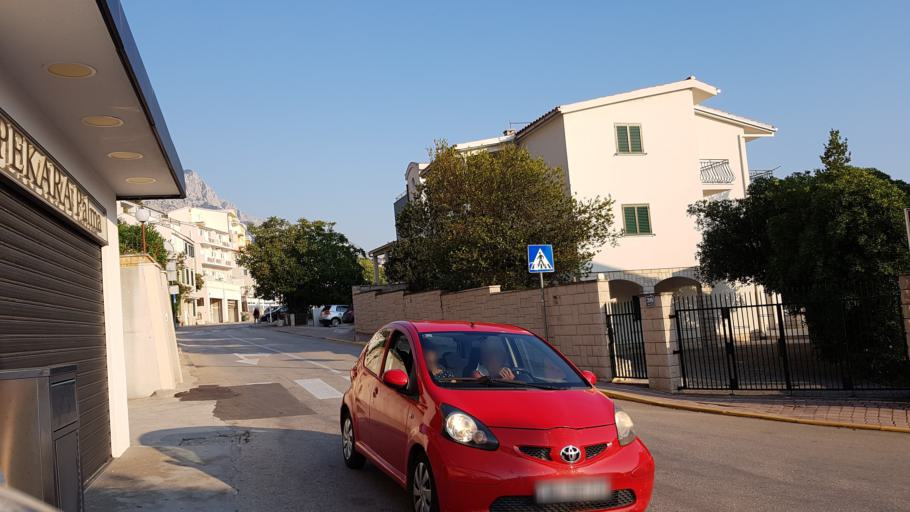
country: HR
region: Splitsko-Dalmatinska
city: Baska Voda
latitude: 43.3593
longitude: 16.9497
